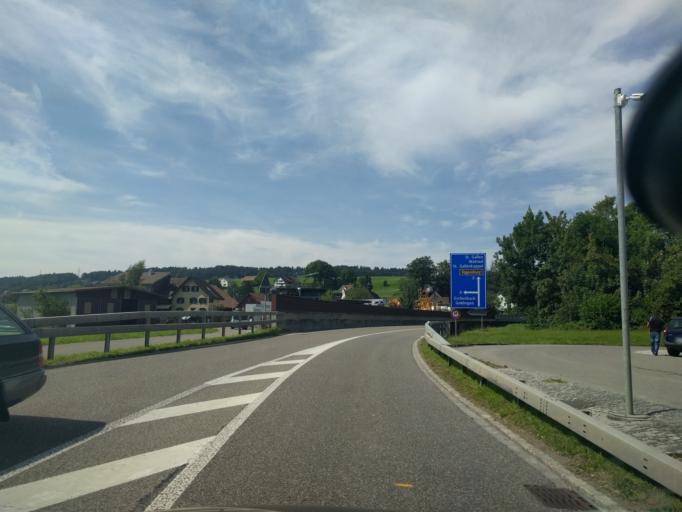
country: CH
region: Saint Gallen
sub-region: Wahlkreis See-Gaster
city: Schmerikon
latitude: 47.2410
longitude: 8.9486
